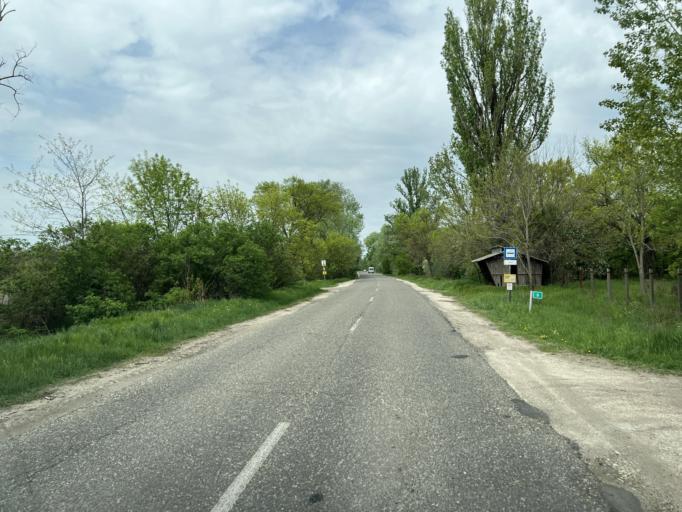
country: HU
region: Pest
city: Tortel
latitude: 47.1344
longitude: 19.9021
